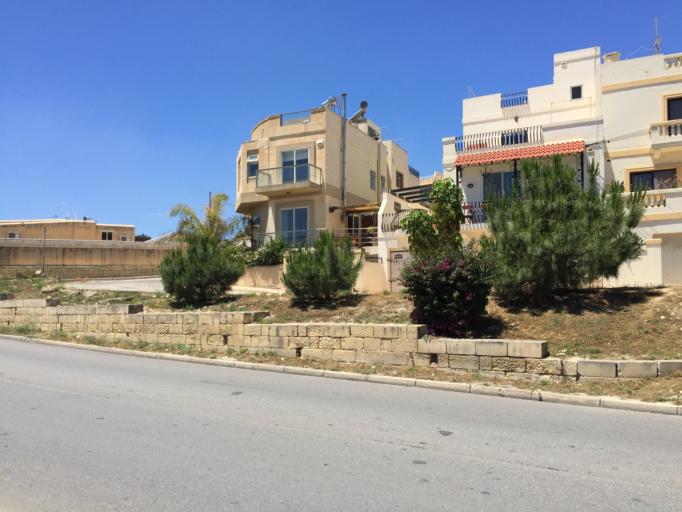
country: MT
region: Is-Swieqi
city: Swieqi
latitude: 35.9253
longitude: 14.4841
